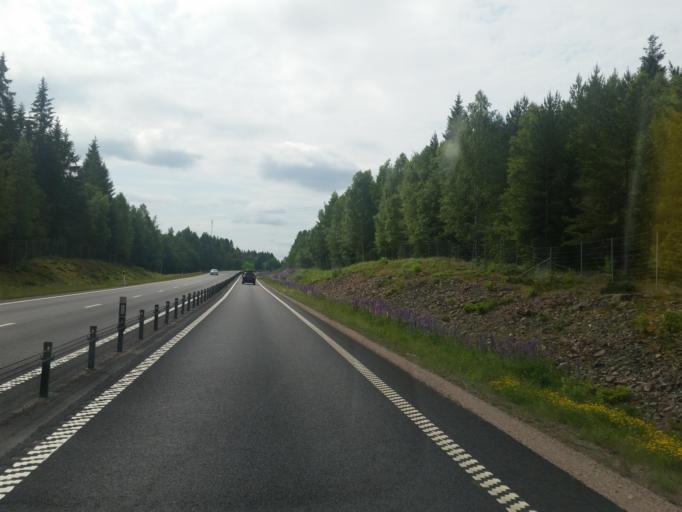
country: SE
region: Dalarna
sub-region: Borlange Kommun
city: Borlaenge
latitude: 60.4527
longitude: 15.3705
